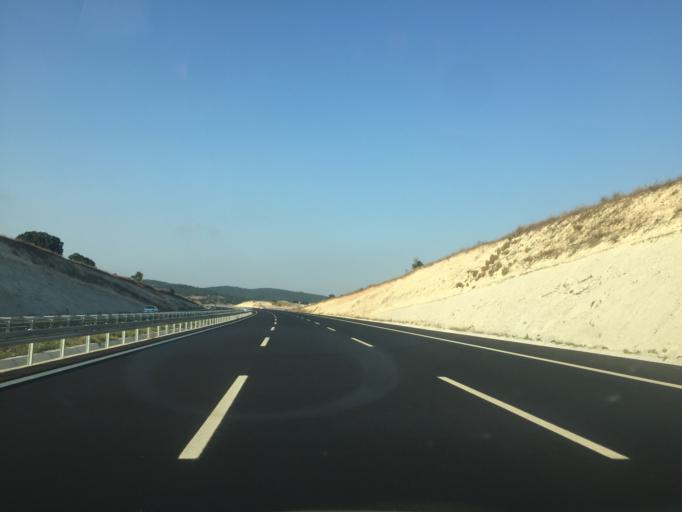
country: TR
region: Balikesir
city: Ertugrul
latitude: 39.4978
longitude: 27.6722
